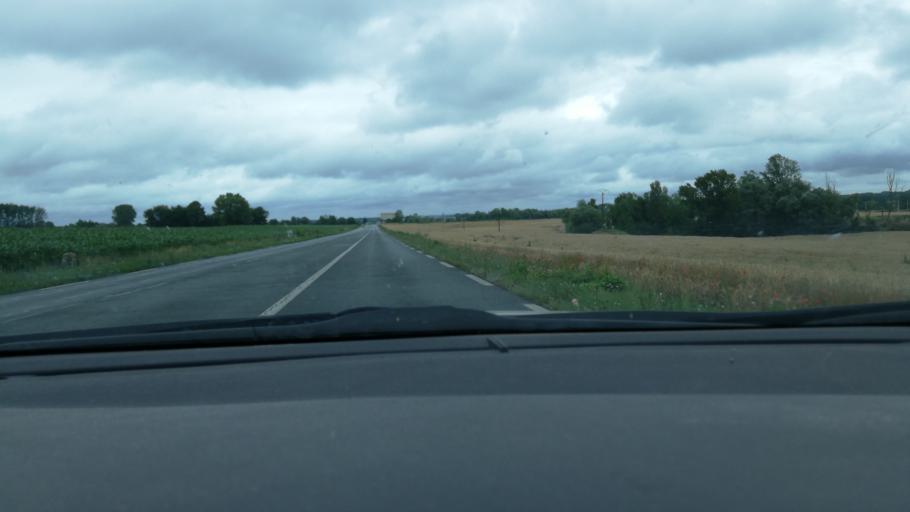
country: FR
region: Poitou-Charentes
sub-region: Departement de la Vienne
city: Naintre
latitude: 46.7408
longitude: 0.4685
